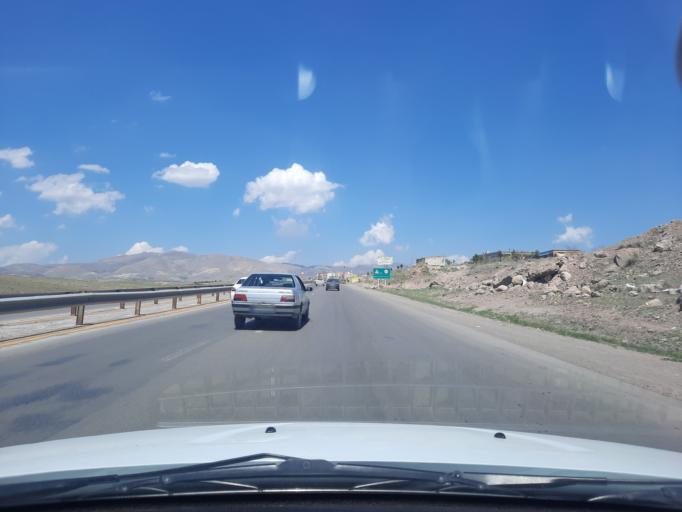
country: IR
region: Qazvin
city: Alvand
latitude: 36.2835
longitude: 50.1302
